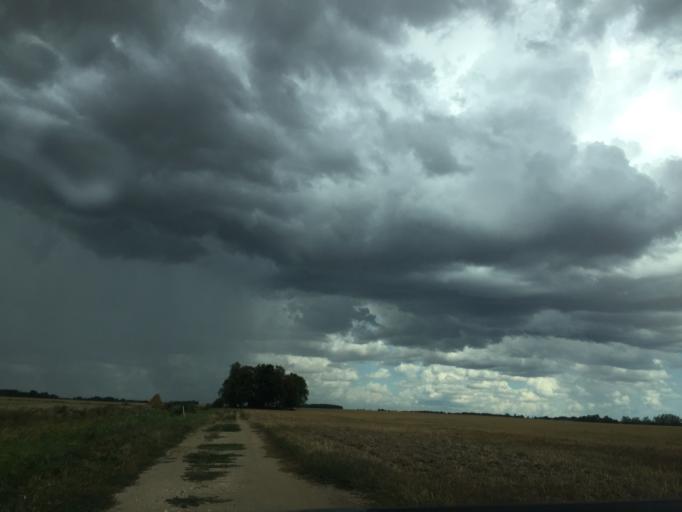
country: LT
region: Siauliu apskritis
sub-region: Joniskis
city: Joniskis
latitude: 56.2913
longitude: 23.7257
